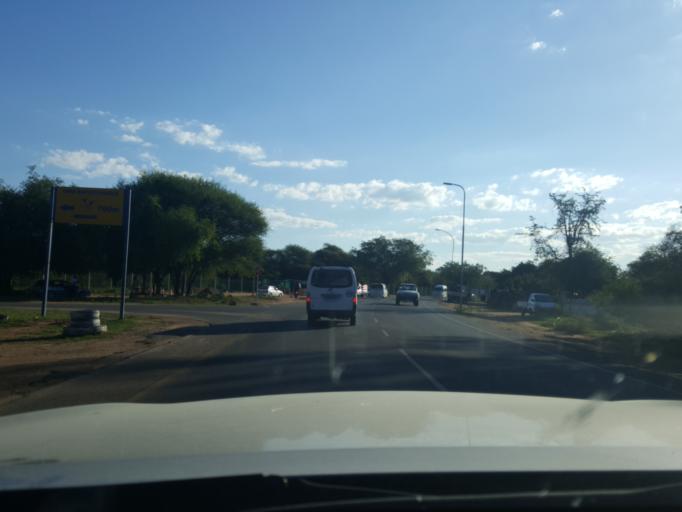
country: BW
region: South East
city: Gaborone
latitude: -24.6445
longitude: 25.9361
